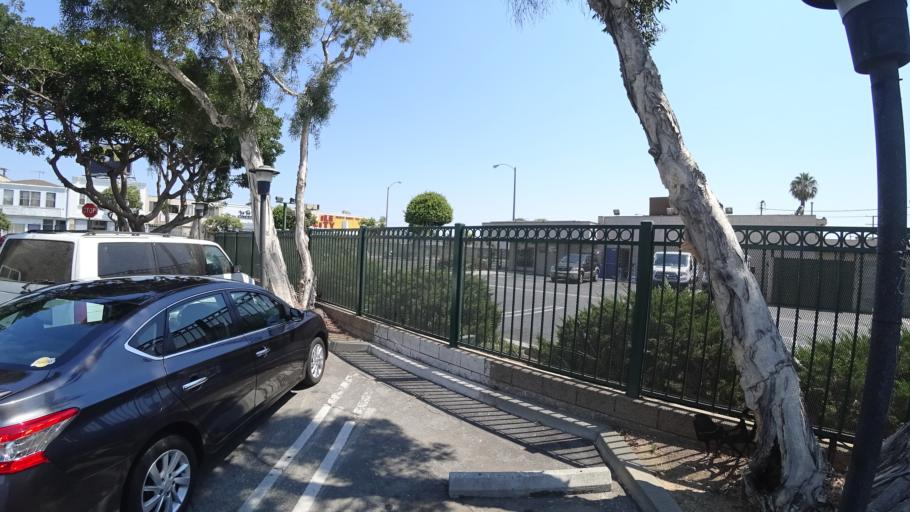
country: US
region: California
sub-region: Los Angeles County
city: Westmont
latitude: 33.9596
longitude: -118.3209
